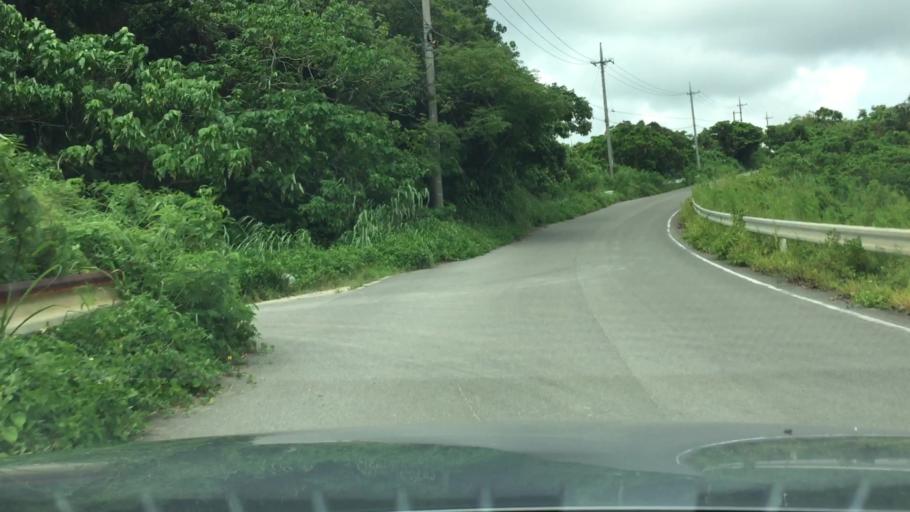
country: JP
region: Okinawa
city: Ishigaki
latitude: 24.3945
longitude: 124.1729
